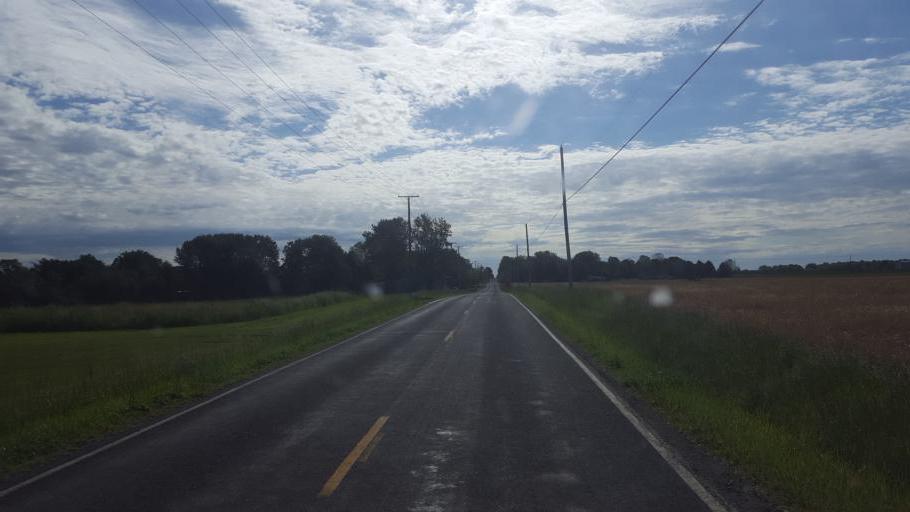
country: US
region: Ohio
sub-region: Medina County
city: Seville
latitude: 41.0471
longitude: -81.8368
